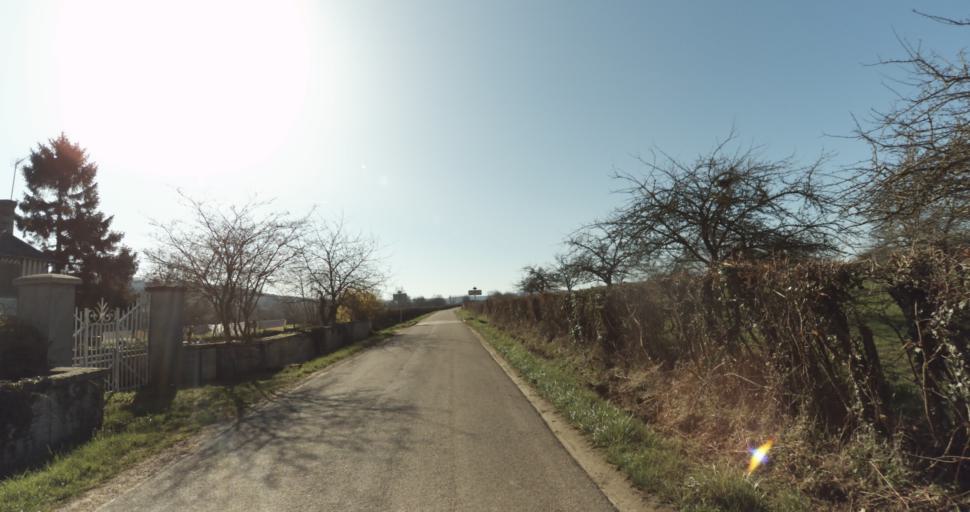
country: FR
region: Lower Normandy
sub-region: Departement du Calvados
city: Saint-Pierre-sur-Dives
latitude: 48.9867
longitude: 0.0301
